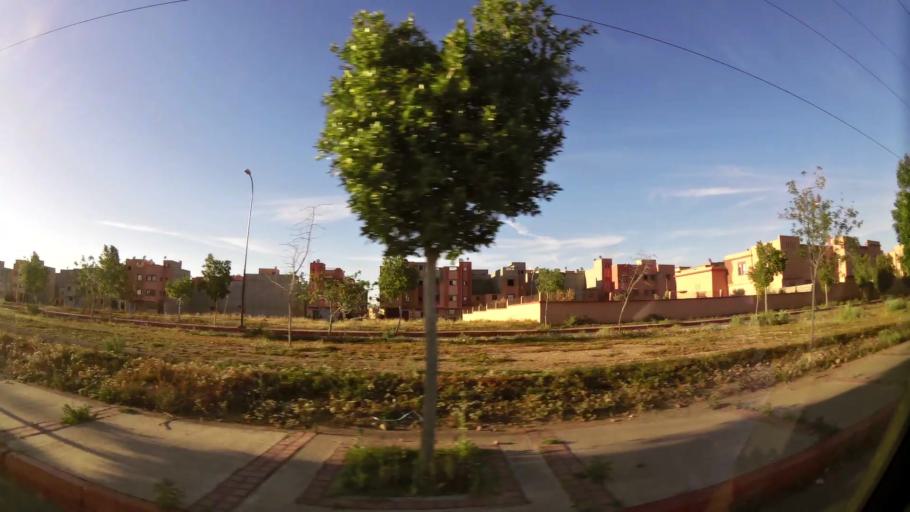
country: MA
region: Marrakech-Tensift-Al Haouz
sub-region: Marrakech
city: Marrakesh
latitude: 31.7428
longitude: -8.1178
